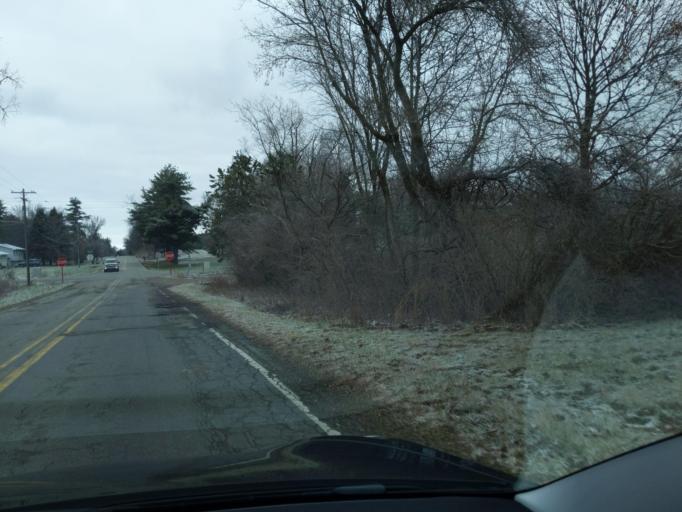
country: US
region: Michigan
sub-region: Jackson County
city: Spring Arbor
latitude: 42.2177
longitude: -84.5165
